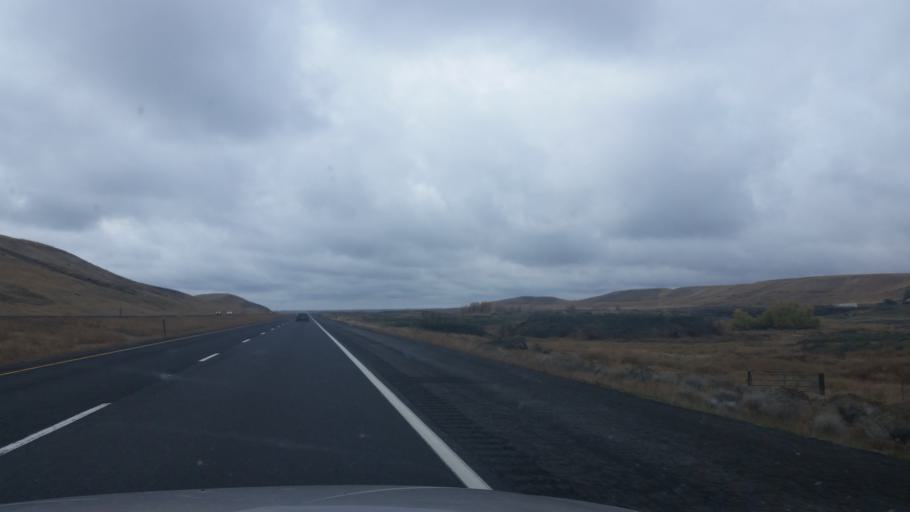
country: US
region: Washington
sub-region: Spokane County
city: Medical Lake
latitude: 47.3582
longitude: -117.8917
